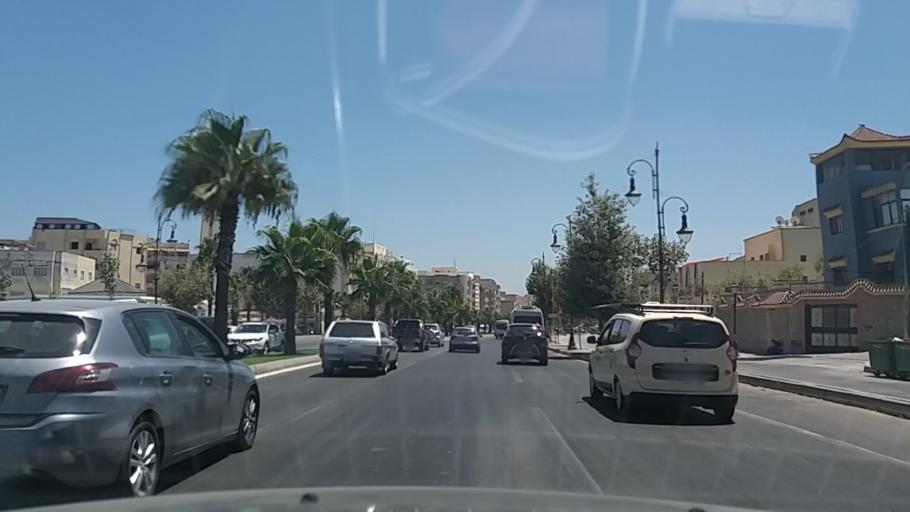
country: MA
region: Tanger-Tetouan
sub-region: Tanger-Assilah
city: Tangier
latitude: 35.7640
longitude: -5.7971
